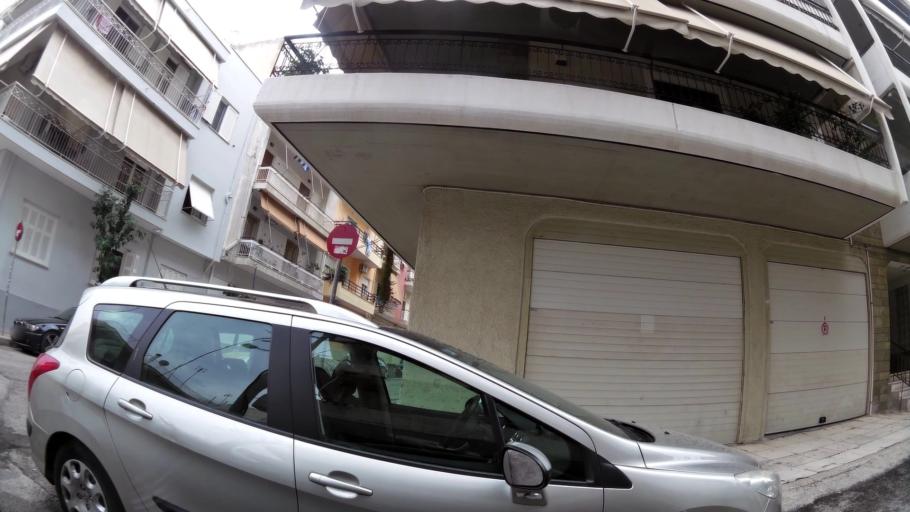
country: GR
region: Attica
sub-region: Nomos Attikis
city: Piraeus
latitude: 37.9297
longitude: 23.6295
